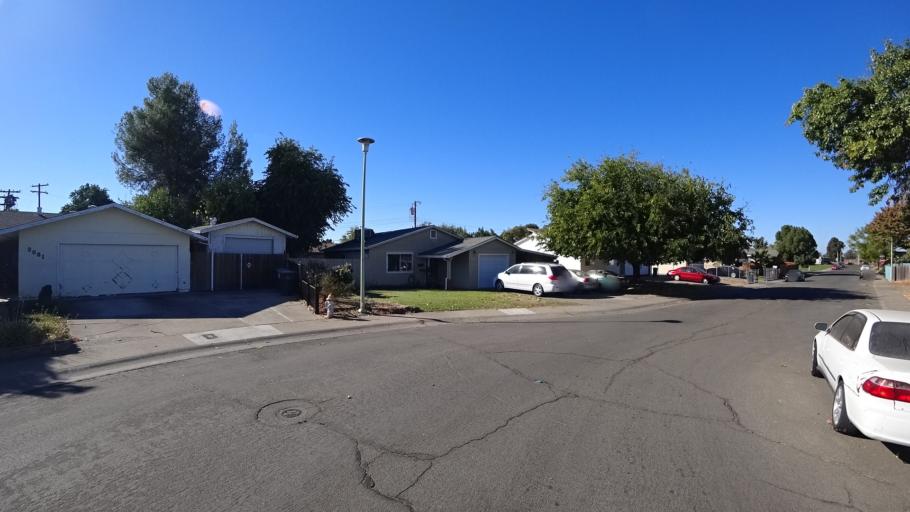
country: US
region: California
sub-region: Sacramento County
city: Parkway
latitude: 38.4725
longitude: -121.4654
